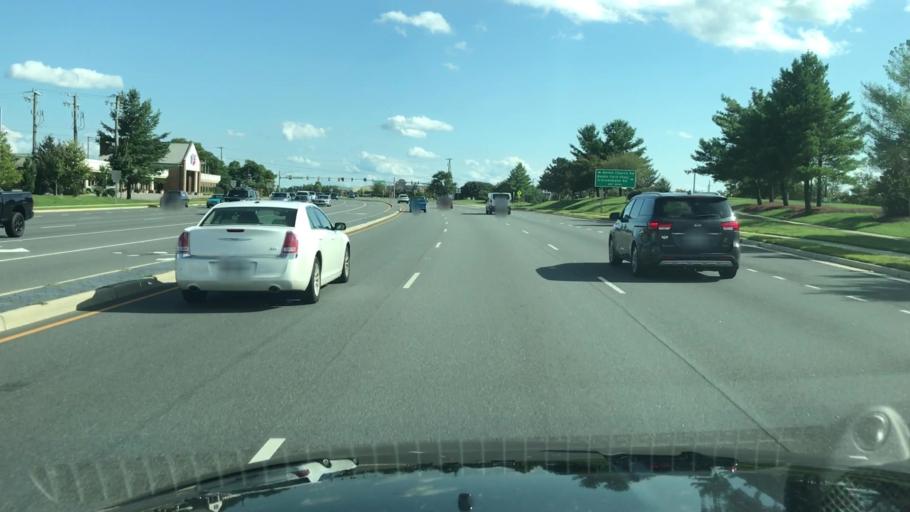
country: US
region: Virginia
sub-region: Stafford County
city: Falmouth
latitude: 38.3640
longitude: -77.5216
